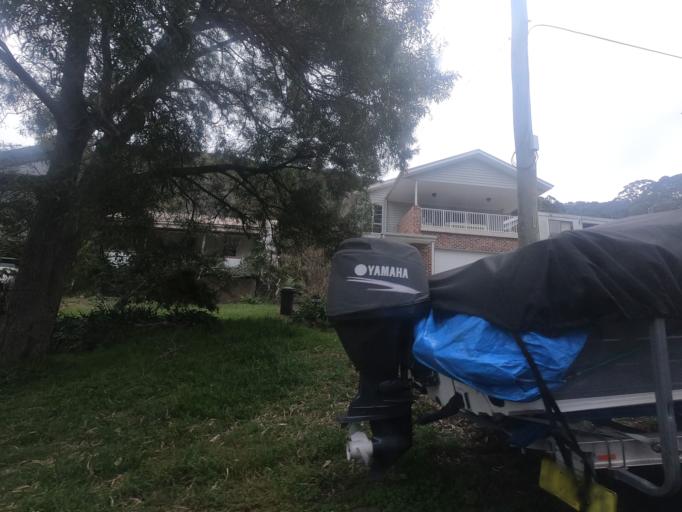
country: AU
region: New South Wales
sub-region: Wollongong
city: Bulli
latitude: -34.2917
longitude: 150.9366
